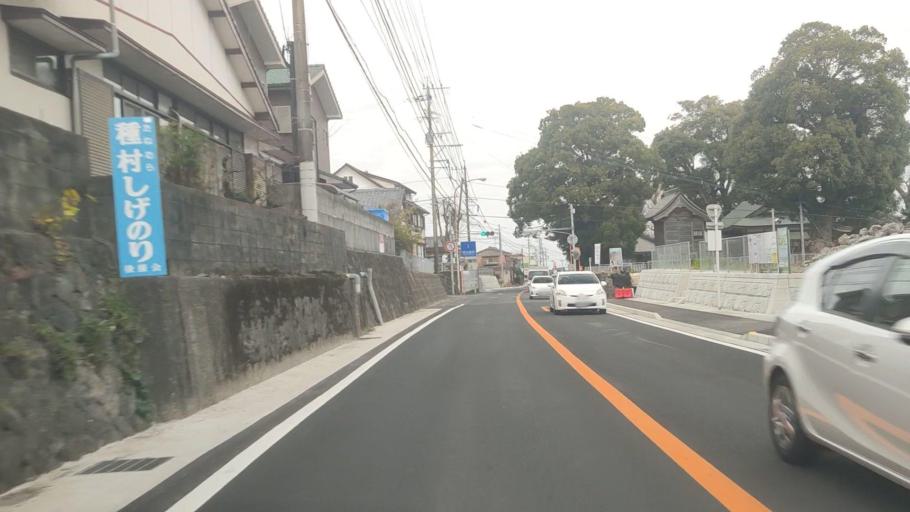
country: JP
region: Nagasaki
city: Shimabara
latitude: 32.8185
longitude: 130.3545
